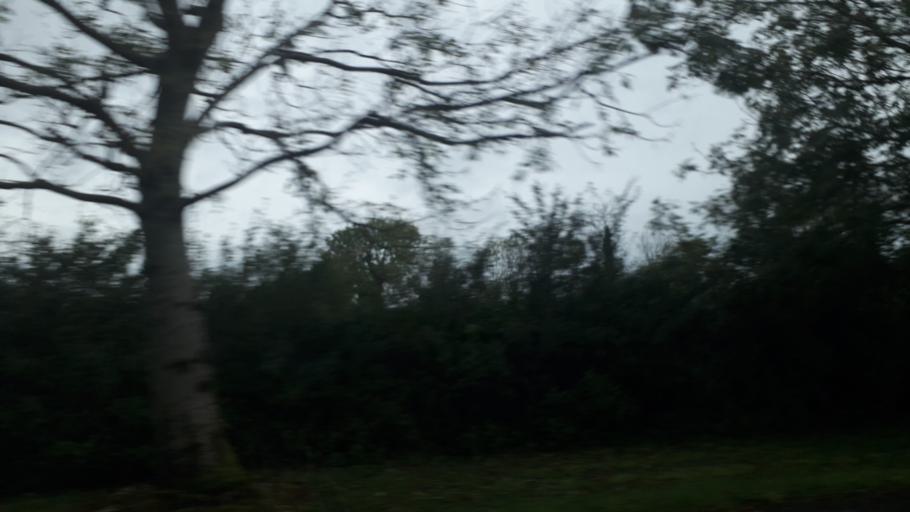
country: IE
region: Leinster
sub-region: An Longfort
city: Lanesborough
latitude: 53.7442
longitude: -7.9302
